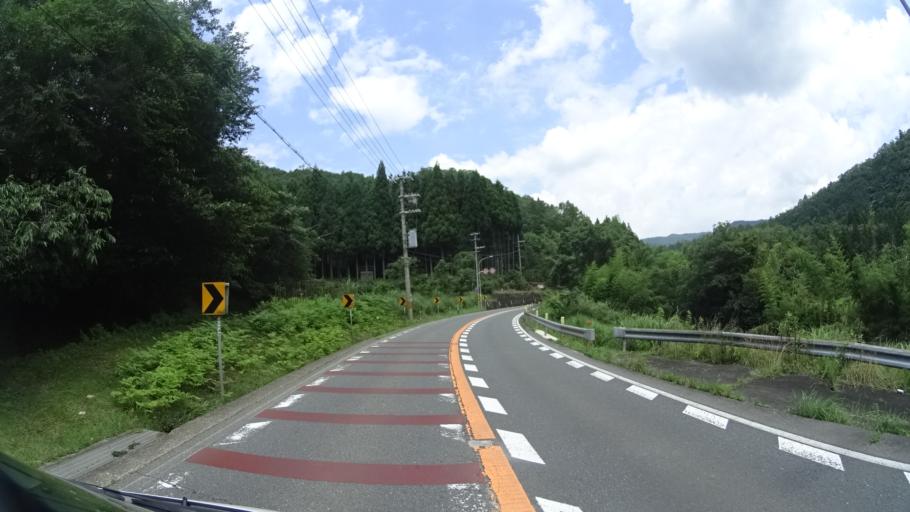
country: JP
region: Kyoto
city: Ayabe
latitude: 35.1972
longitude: 135.2837
